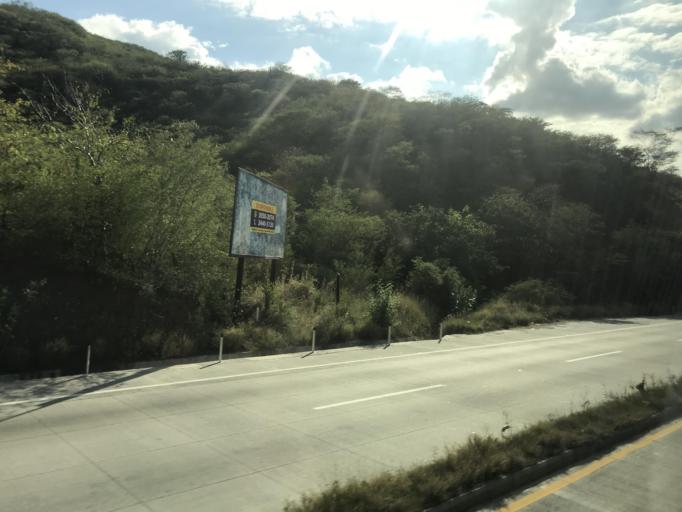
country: GT
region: El Progreso
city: Guastatoya
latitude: 14.8541
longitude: -90.0950
